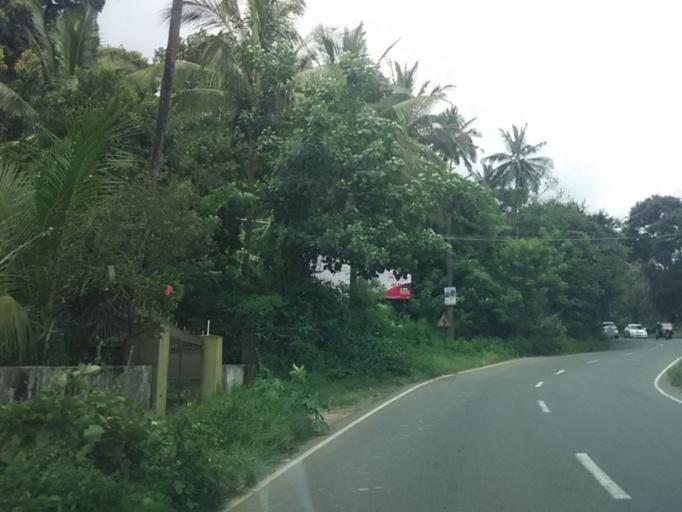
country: IN
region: Kerala
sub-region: Wayanad
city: Kalpetta
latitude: 11.5789
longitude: 76.0608
